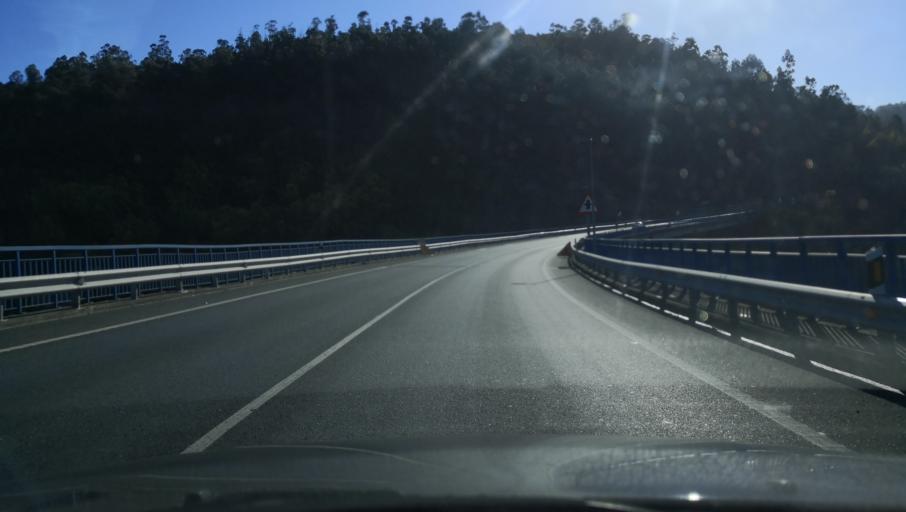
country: ES
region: Galicia
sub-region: Provincia da Coruna
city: Ribeira
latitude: 42.7772
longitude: -8.4029
